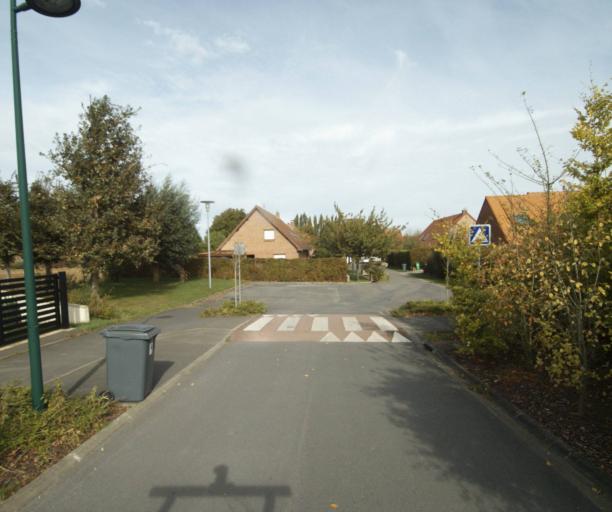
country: FR
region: Nord-Pas-de-Calais
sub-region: Departement du Nord
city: Radinghem-en-Weppes
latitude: 50.6208
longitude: 2.9048
